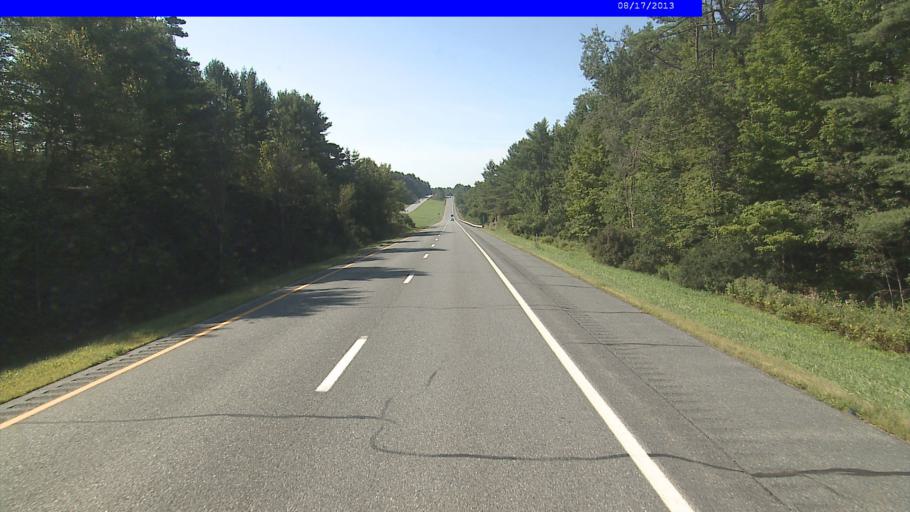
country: US
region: Vermont
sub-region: Windsor County
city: Springfield
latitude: 43.3198
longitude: -72.4207
